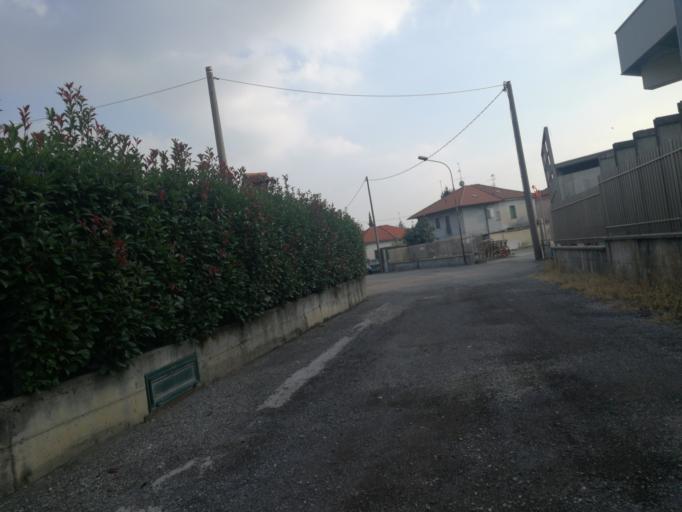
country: IT
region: Lombardy
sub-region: Provincia di Monza e Brianza
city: Porto d'Adda
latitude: 45.6535
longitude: 9.4630
